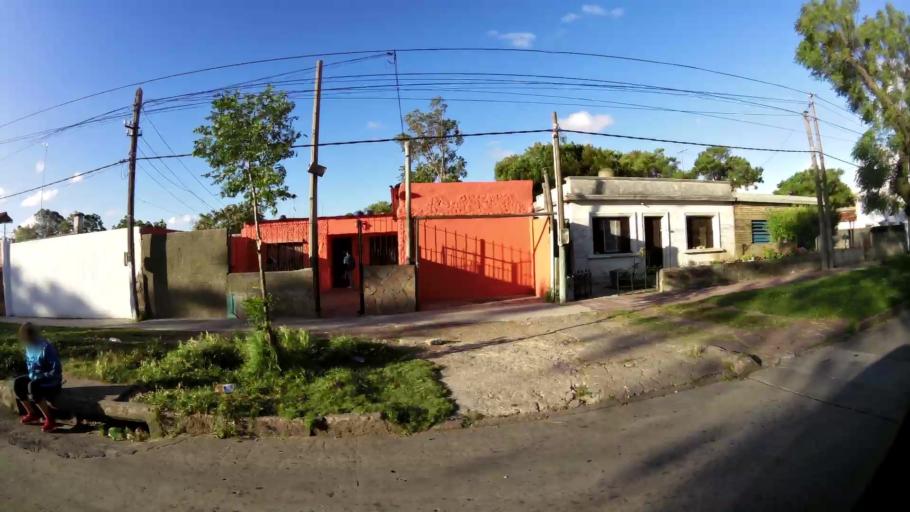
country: UY
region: Montevideo
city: Montevideo
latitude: -34.8657
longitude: -56.1414
